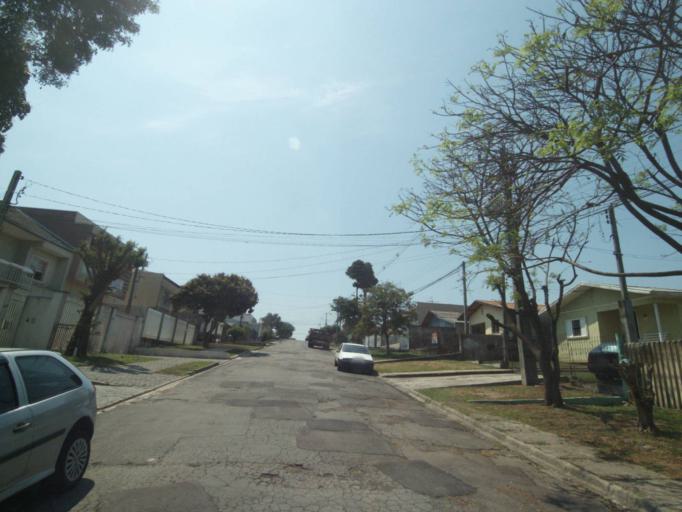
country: BR
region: Parana
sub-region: Sao Jose Dos Pinhais
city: Sao Jose dos Pinhais
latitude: -25.5166
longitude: -49.2685
